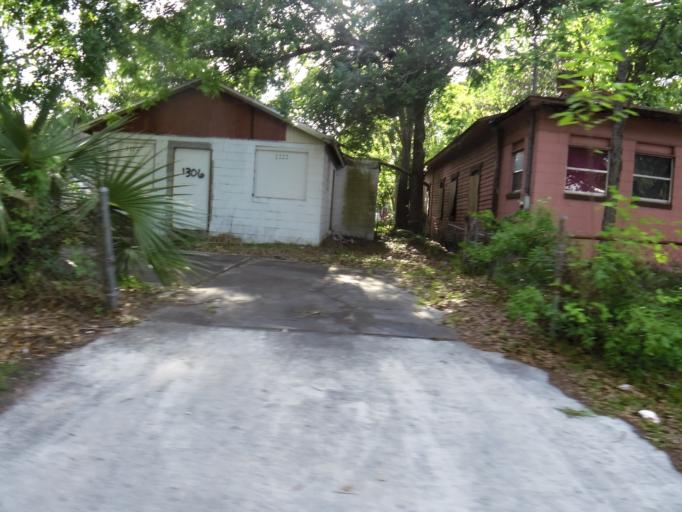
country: US
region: Florida
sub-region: Duval County
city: Jacksonville
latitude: 30.3414
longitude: -81.6806
